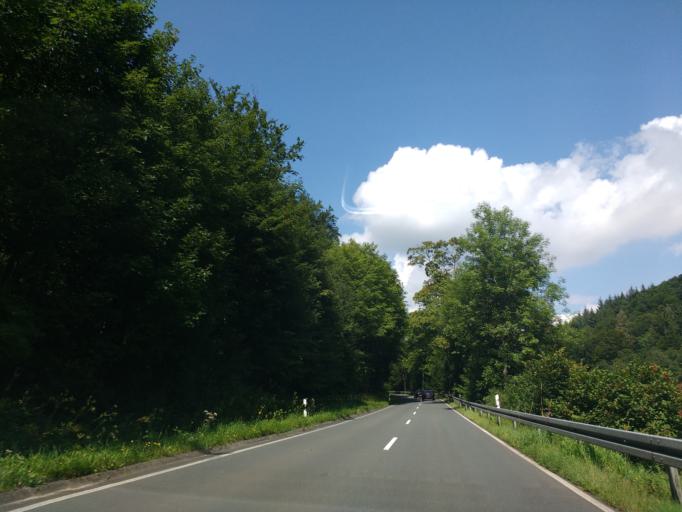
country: DE
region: Hesse
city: Dillenburg
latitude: 50.7108
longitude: 8.2492
